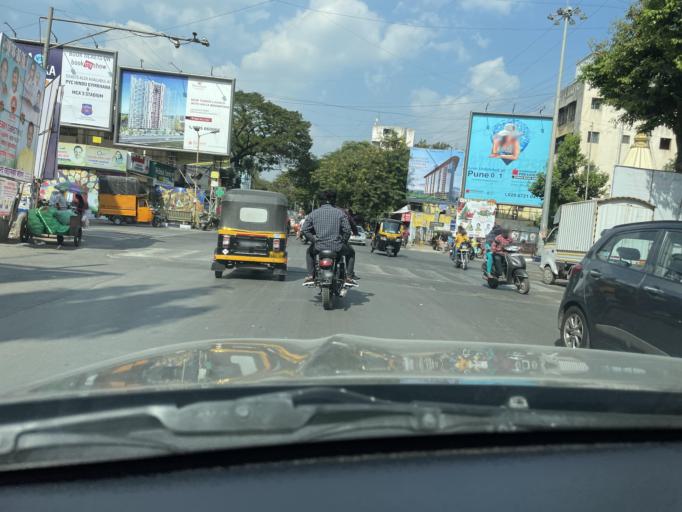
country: IN
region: Maharashtra
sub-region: Pune Division
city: Pune
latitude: 18.4919
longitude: 73.9000
